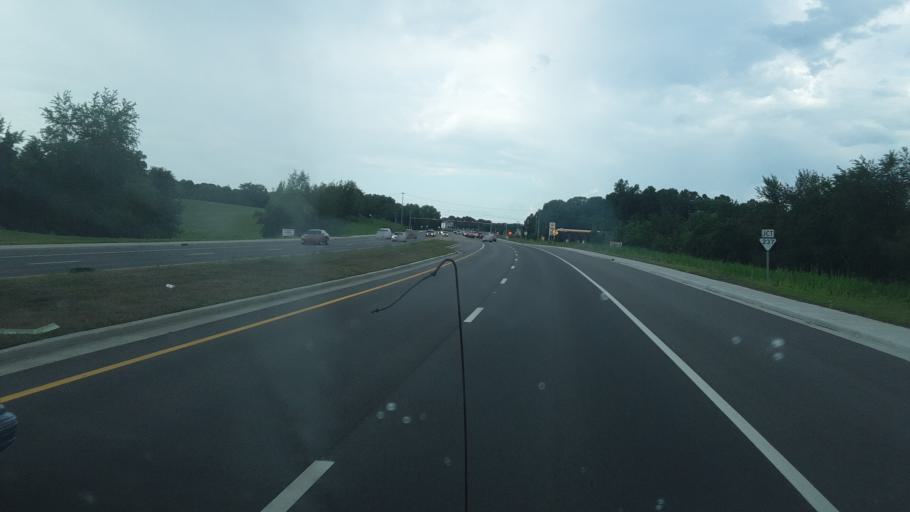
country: US
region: Tennessee
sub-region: Montgomery County
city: Clarksville
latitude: 36.5576
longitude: -87.2877
